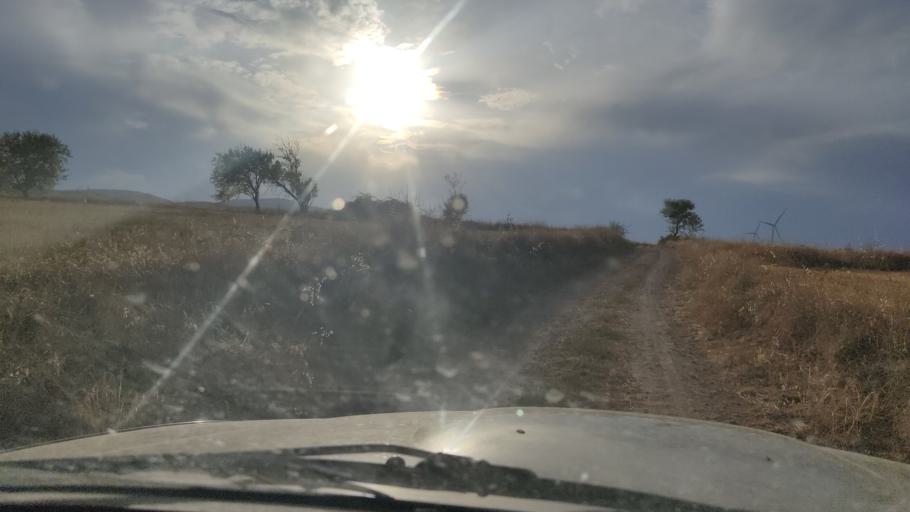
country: ES
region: Aragon
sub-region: Provincia de Teruel
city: Monforte de Moyuela
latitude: 41.0659
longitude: -0.9868
